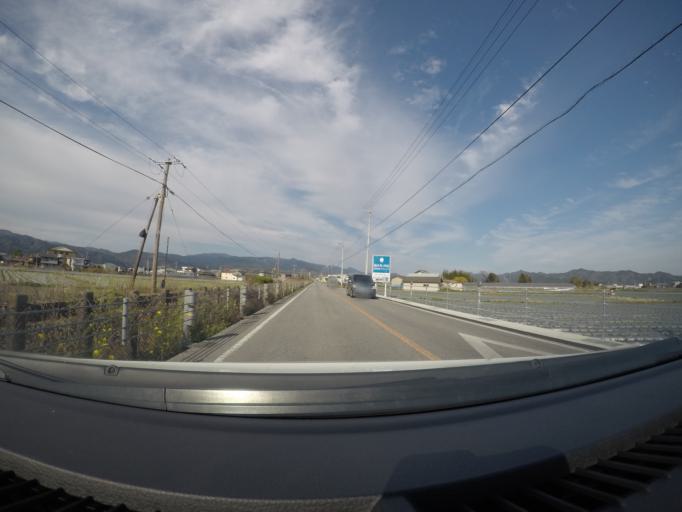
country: JP
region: Kochi
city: Kochi-shi
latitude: 33.5969
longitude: 133.6682
